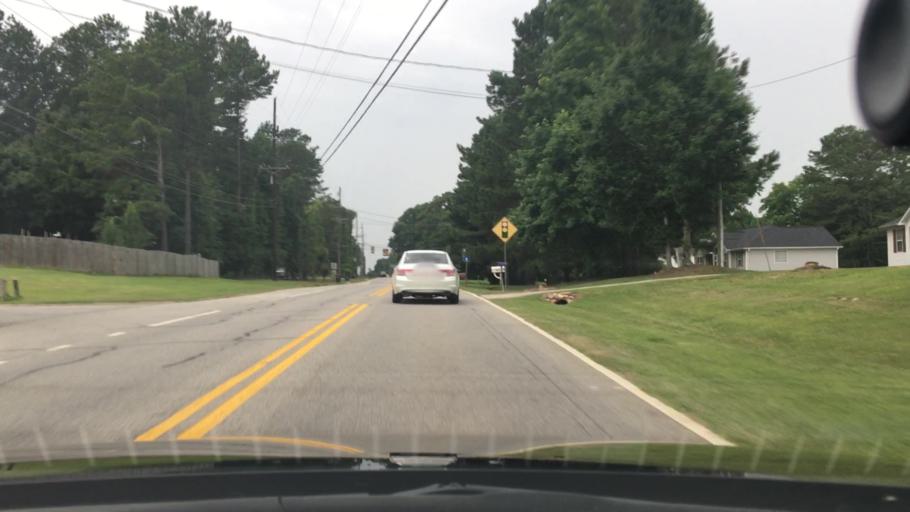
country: US
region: Georgia
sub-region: Coweta County
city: East Newnan
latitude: 33.3557
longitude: -84.7106
